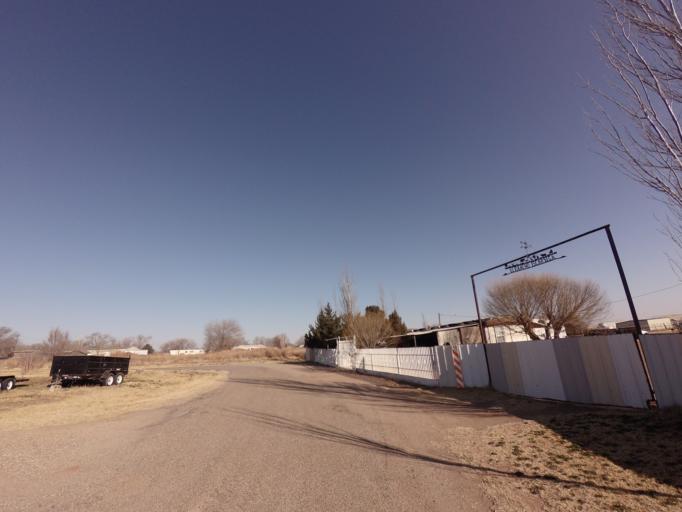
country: US
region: New Mexico
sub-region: Curry County
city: Clovis
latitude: 34.3852
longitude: -103.1810
